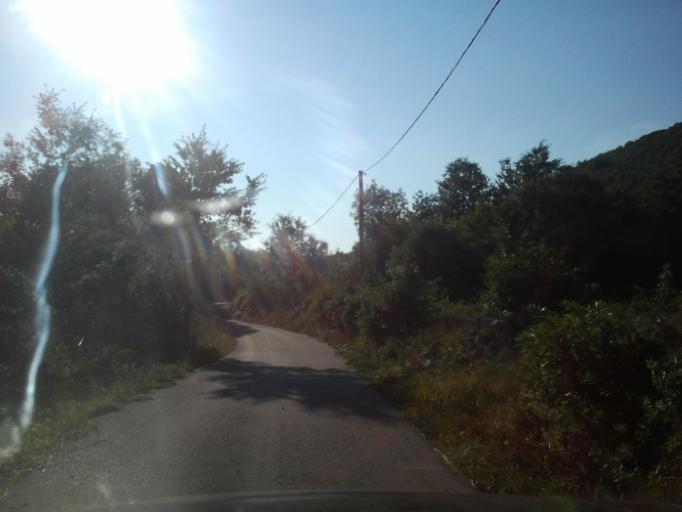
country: HR
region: Zadarska
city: Gracac
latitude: 44.3622
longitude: 15.7162
